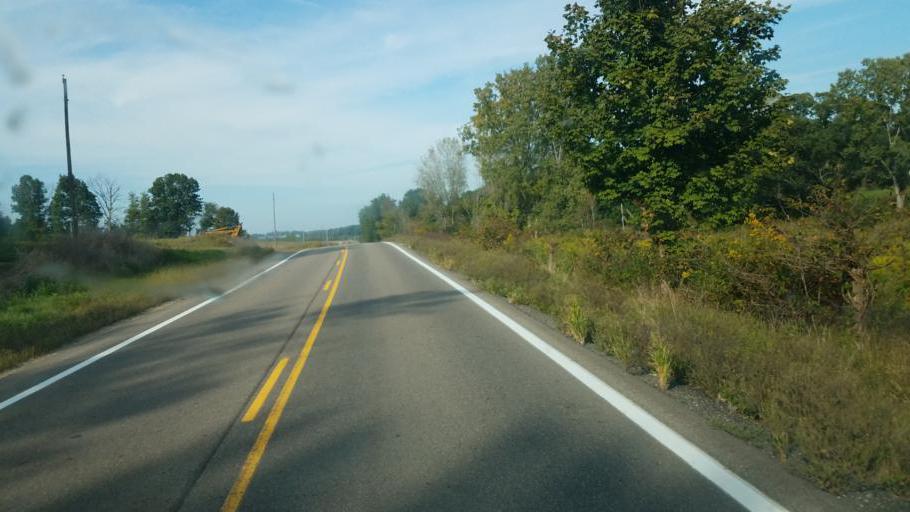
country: US
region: Ohio
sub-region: Knox County
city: Gambier
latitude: 40.2940
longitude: -82.3369
